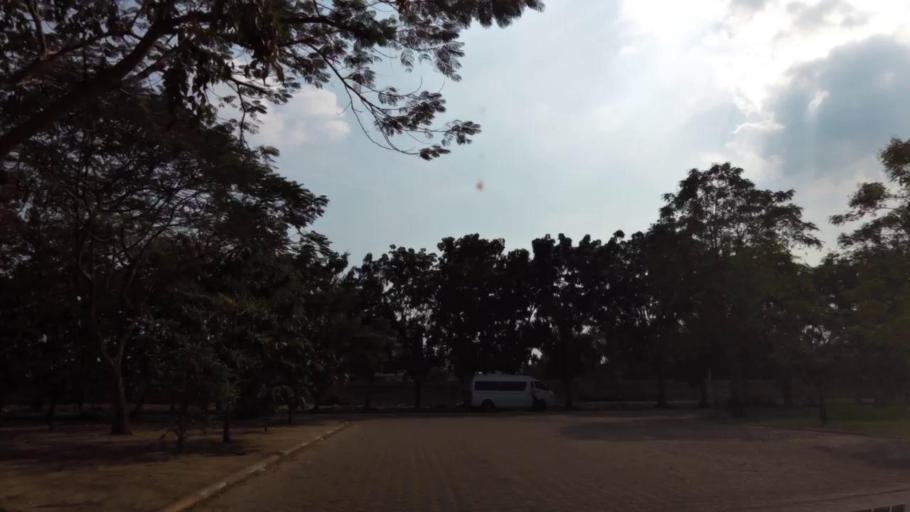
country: TH
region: Phra Nakhon Si Ayutthaya
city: Phra Nakhon Si Ayutthaya
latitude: 14.3425
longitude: 100.5939
